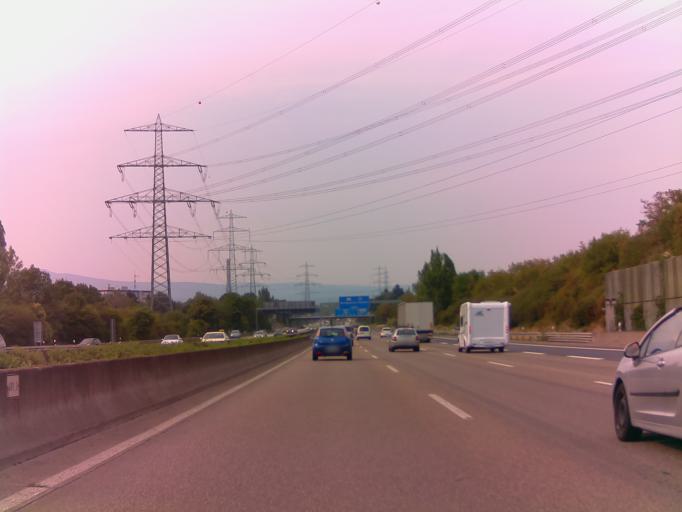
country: DE
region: Hesse
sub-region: Regierungsbezirk Darmstadt
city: Eschborn
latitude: 50.1175
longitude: 8.5972
